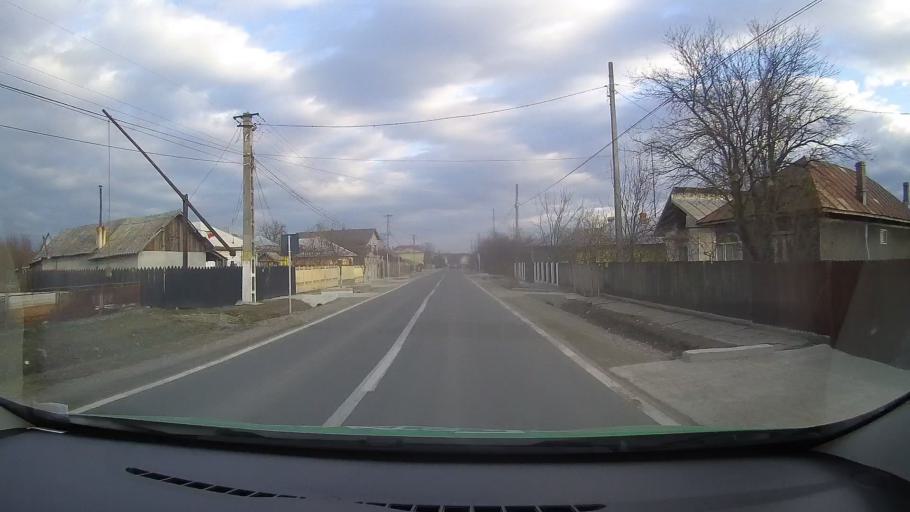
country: RO
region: Dambovita
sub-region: Comuna I. L. Caragiale
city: Ghirdoveni
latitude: 44.9381
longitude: 25.6806
